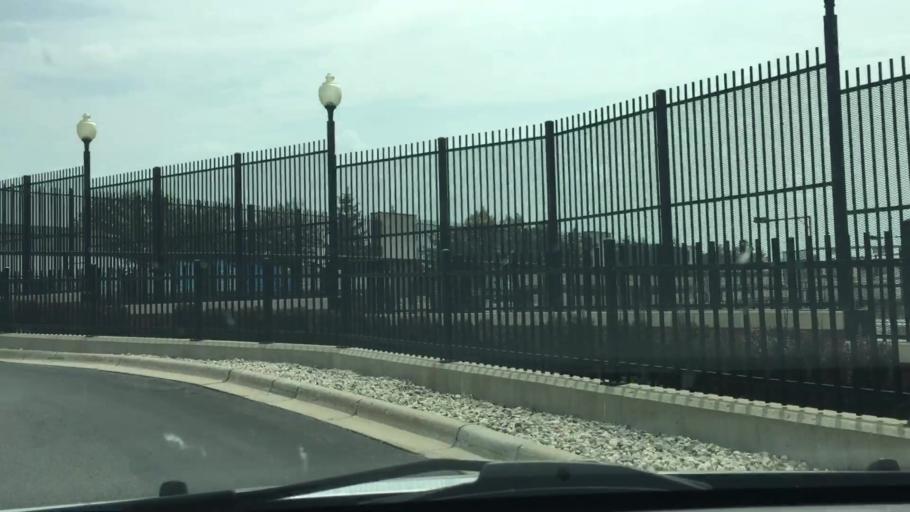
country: US
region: Wisconsin
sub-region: Waukesha County
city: Waukesha
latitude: 43.0352
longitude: -88.1797
